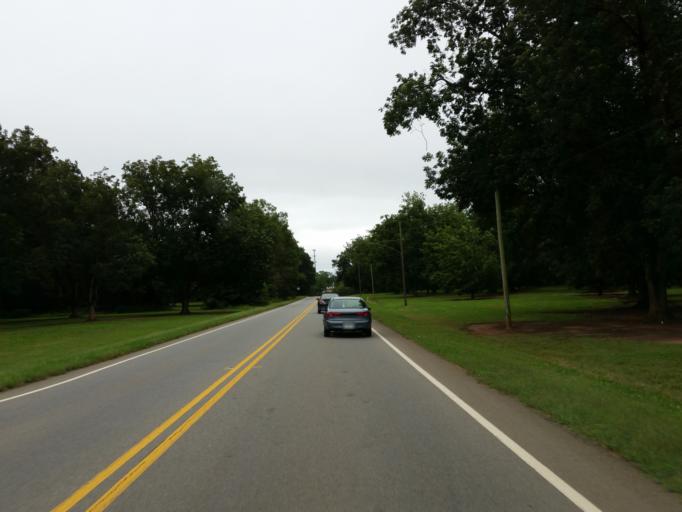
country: US
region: Georgia
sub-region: Peach County
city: Fort Valley
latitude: 32.5671
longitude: -83.8867
